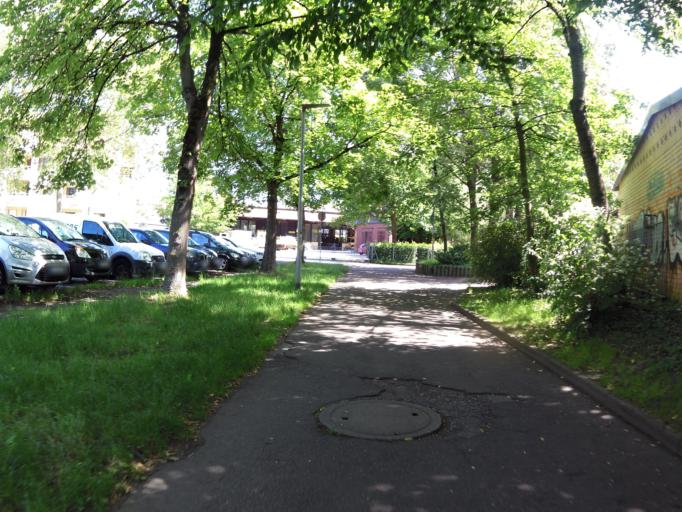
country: DE
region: Baden-Wuerttemberg
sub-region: Freiburg Region
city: Lahr
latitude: 48.3392
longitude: 7.8778
